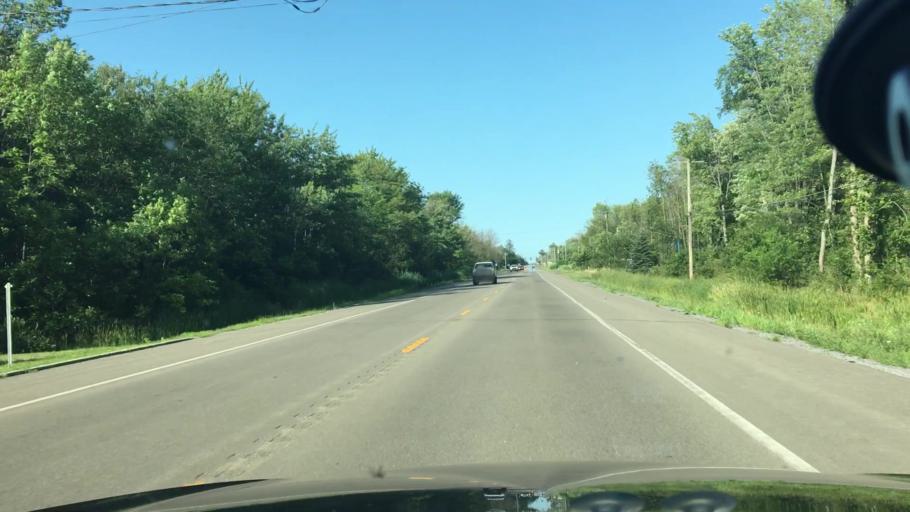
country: US
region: New York
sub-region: Erie County
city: Wanakah
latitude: 42.7041
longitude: -78.9247
